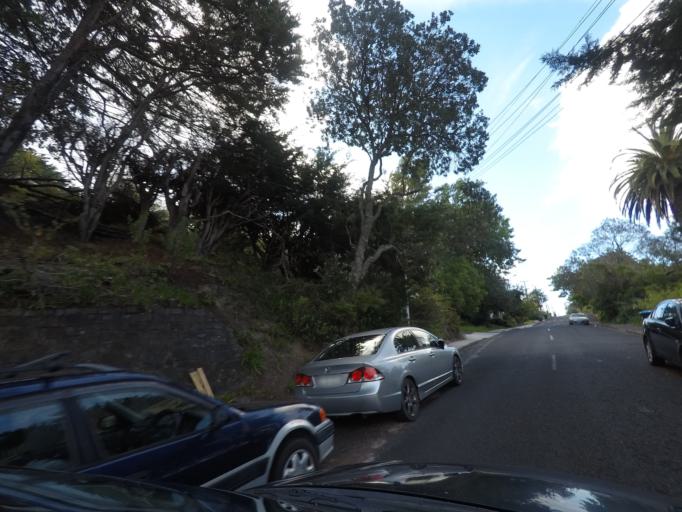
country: NZ
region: Auckland
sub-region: Auckland
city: Auckland
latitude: -36.9247
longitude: 174.7583
